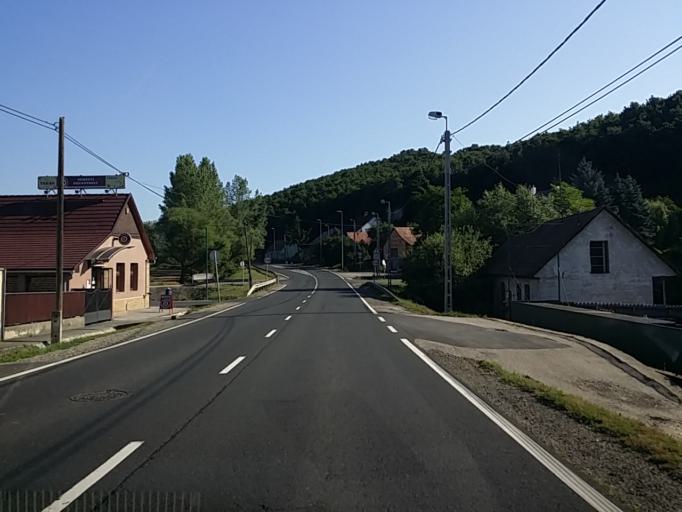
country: HU
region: Nograd
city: Retsag
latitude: 47.8581
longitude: 19.1061
